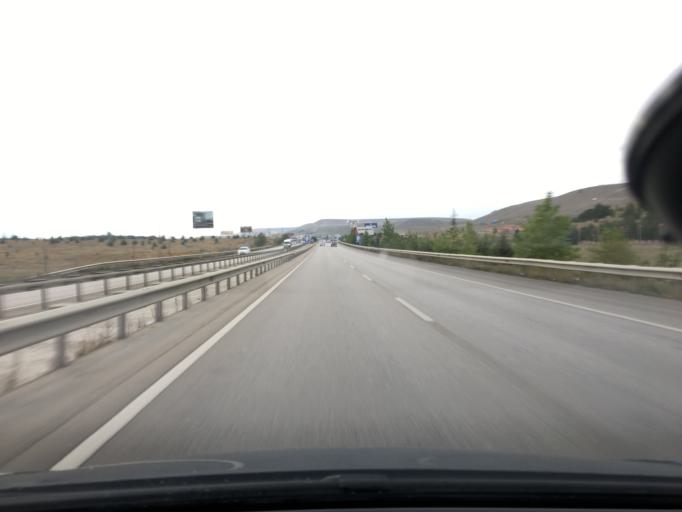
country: TR
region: Afyonkarahisar
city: Afyonkarahisar
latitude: 38.7932
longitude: 30.4092
